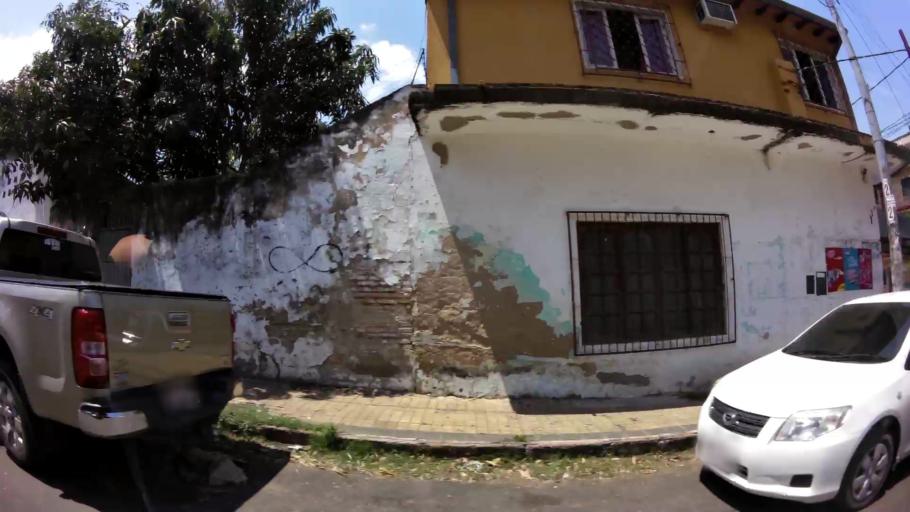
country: PY
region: Asuncion
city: Asuncion
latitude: -25.3019
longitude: -57.6485
